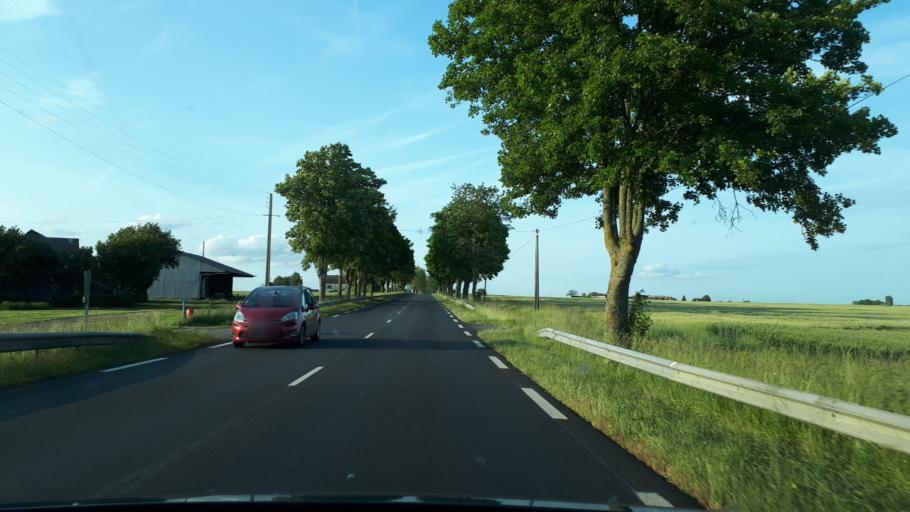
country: FR
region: Centre
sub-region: Departement du Loir-et-Cher
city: Naveil
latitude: 47.7476
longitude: 1.0405
